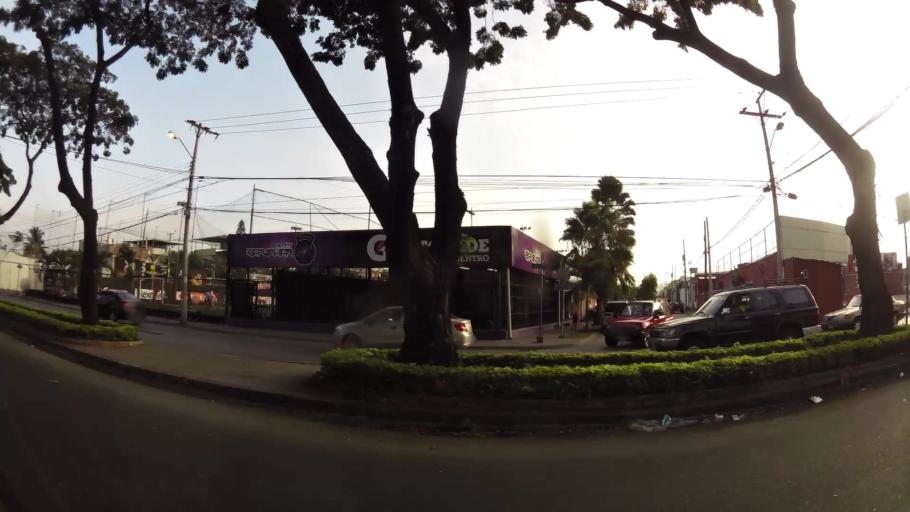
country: EC
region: Guayas
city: Eloy Alfaro
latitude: -2.1423
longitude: -79.8888
